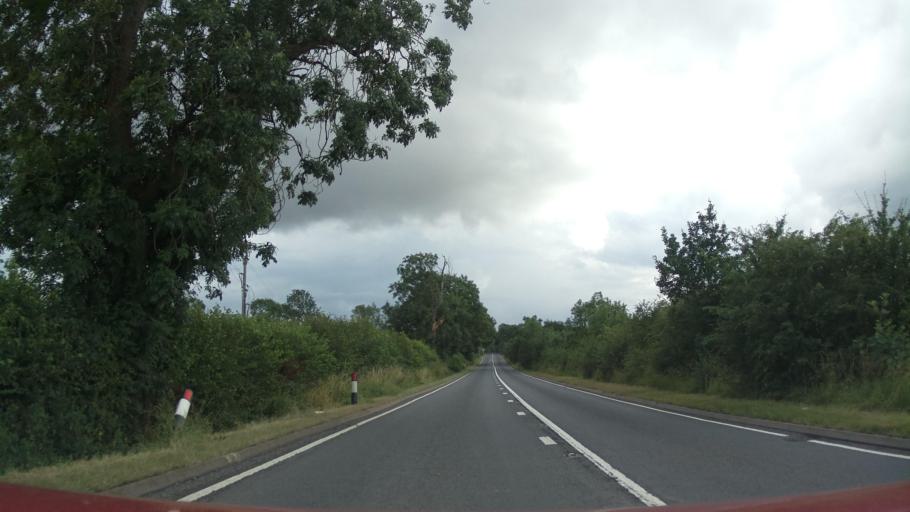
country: GB
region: England
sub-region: Warwickshire
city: Long Itchington
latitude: 52.2782
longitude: -1.3617
